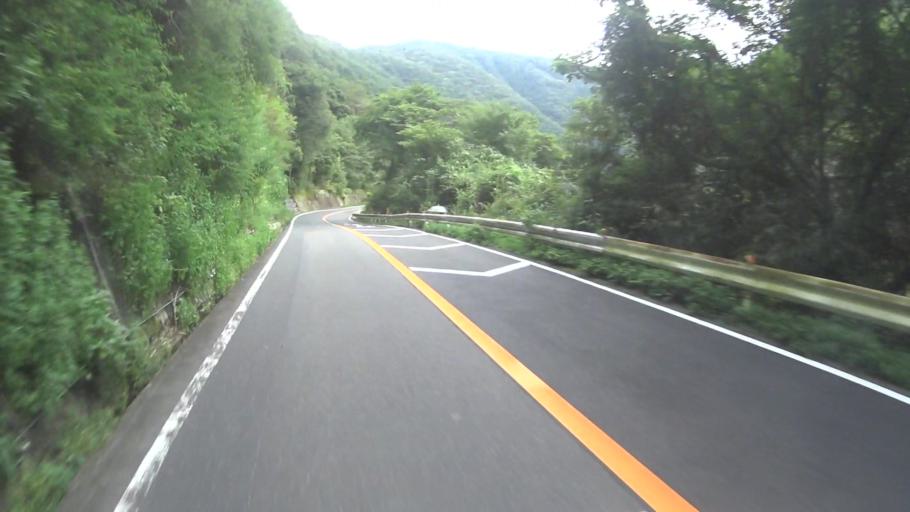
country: JP
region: Kyoto
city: Uji
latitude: 34.8989
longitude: 135.8670
